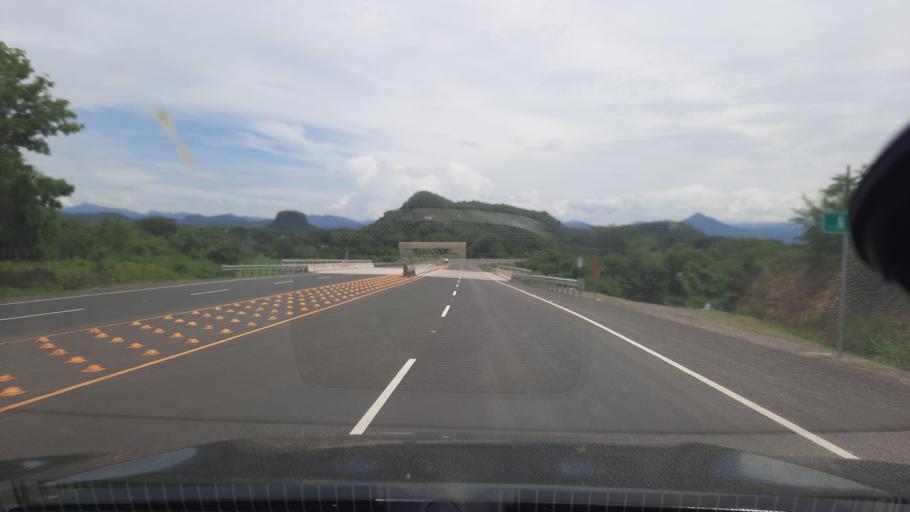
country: HN
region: Valle
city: Aramecina
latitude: 13.7162
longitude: -87.7074
